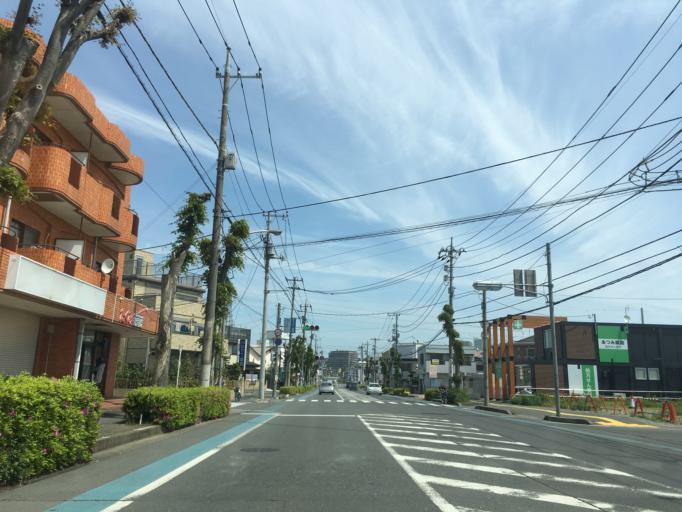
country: JP
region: Saitama
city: Ageoshimo
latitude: 35.9659
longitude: 139.5787
